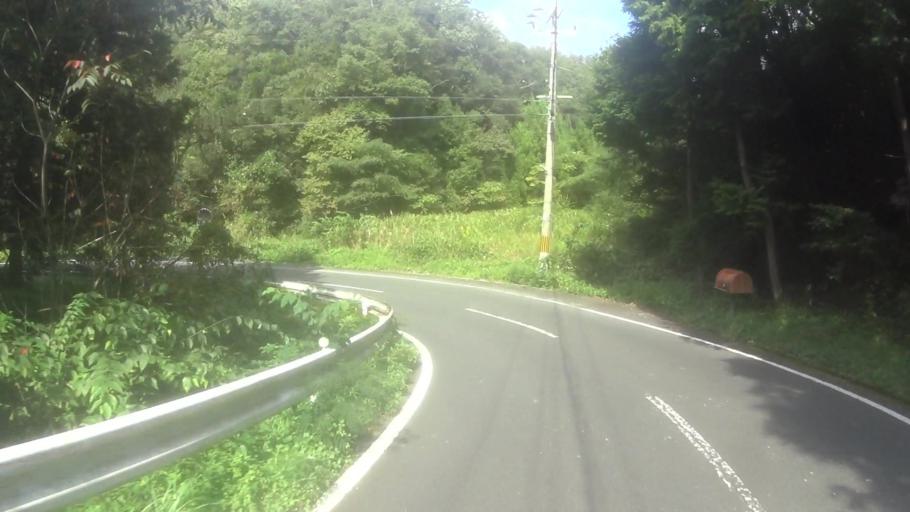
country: JP
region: Kyoto
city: Miyazu
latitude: 35.5878
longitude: 135.1164
